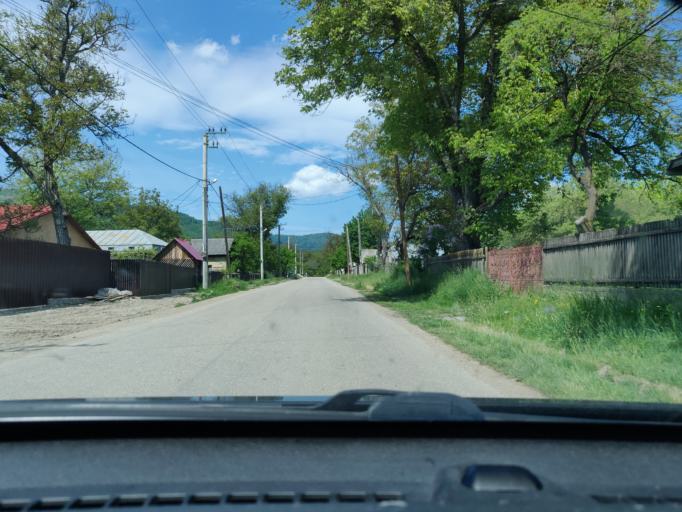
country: RO
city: Vizantea-Manastireasca
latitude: 45.9790
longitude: 26.8023
